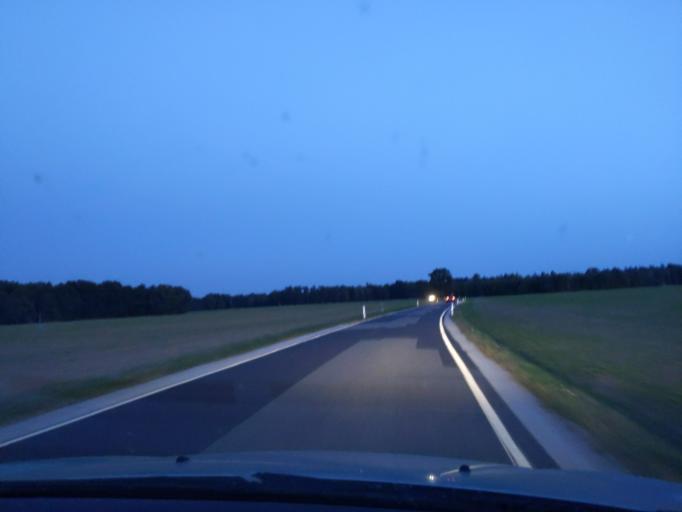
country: DE
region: Saxony
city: Grossdubrau
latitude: 51.2914
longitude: 14.4693
